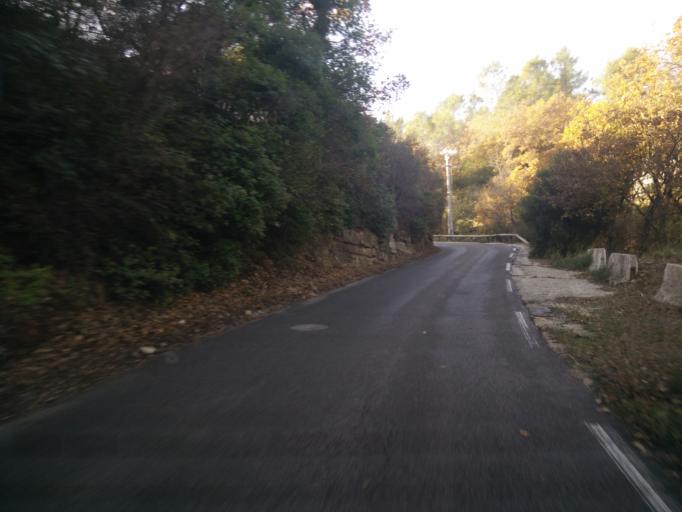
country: FR
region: Provence-Alpes-Cote d'Azur
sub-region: Departement du Var
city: Sollies-Toucas
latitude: 43.2043
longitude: 6.0088
